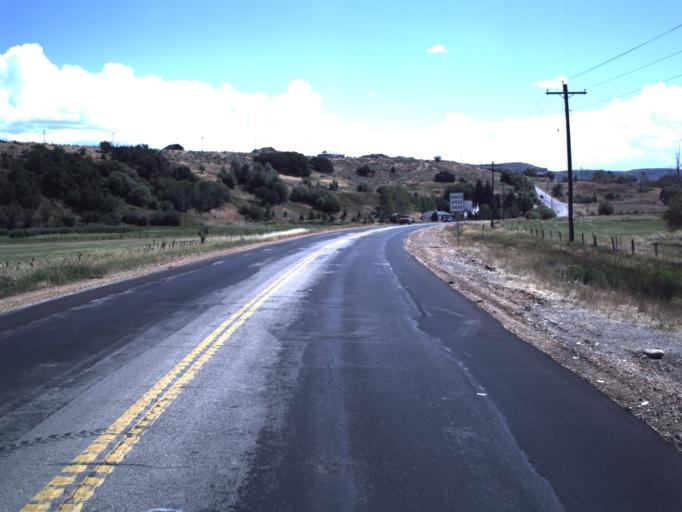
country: US
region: Utah
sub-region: Summit County
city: Francis
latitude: 40.6120
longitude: -111.2985
